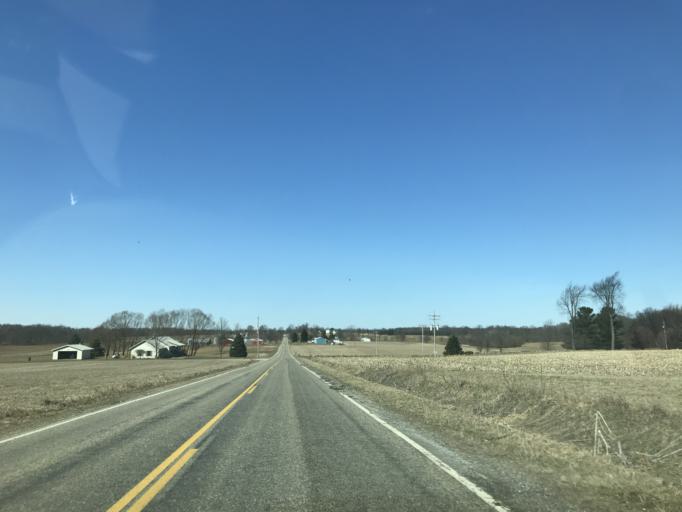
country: US
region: Michigan
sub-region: Hillsdale County
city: Jonesville
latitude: 41.9855
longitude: -84.6978
